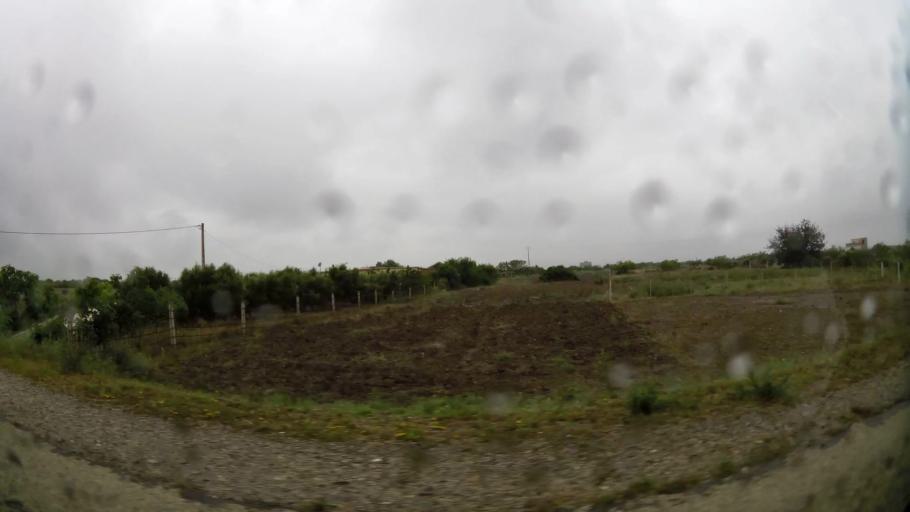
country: MA
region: Taza-Al Hoceima-Taounate
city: Imzourene
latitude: 35.1331
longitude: -3.7815
